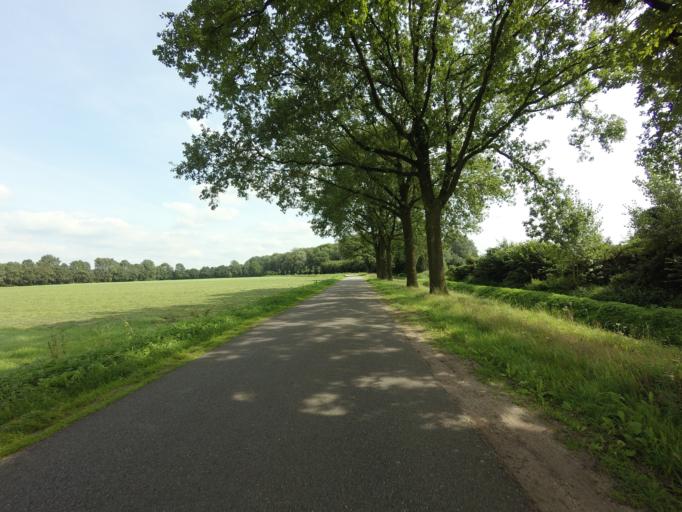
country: DE
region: Lower Saxony
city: Lage
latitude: 52.3965
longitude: 6.9216
